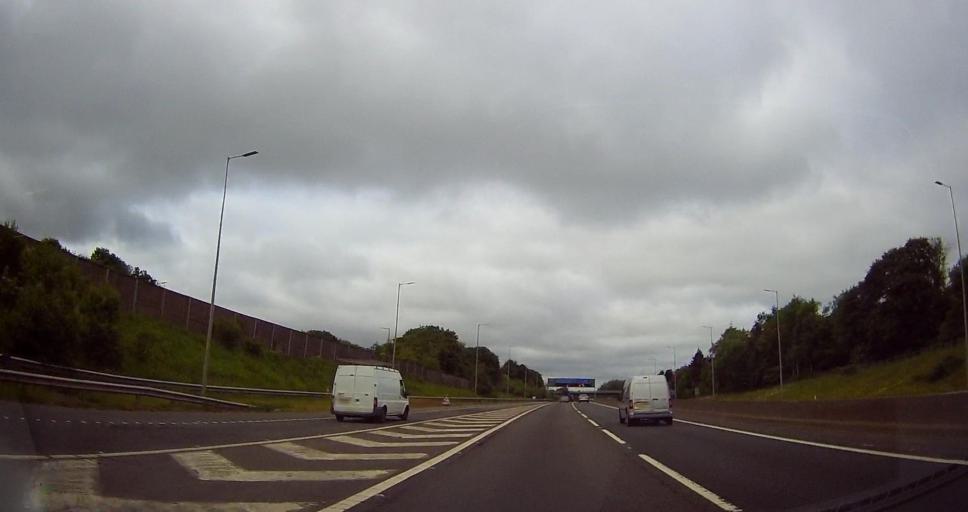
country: GB
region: Scotland
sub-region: North Lanarkshire
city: Cumbernauld
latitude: 55.9389
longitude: -4.0207
